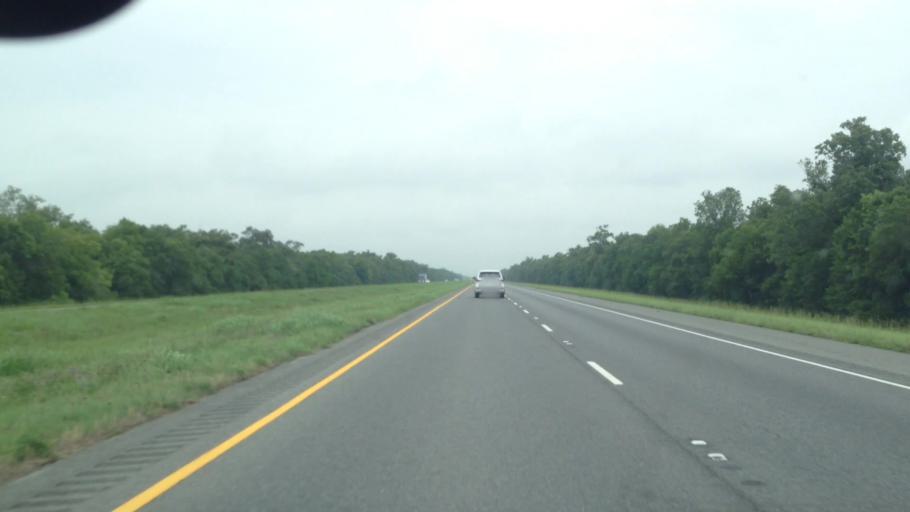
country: US
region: Louisiana
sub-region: Evangeline Parish
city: Ville Platte
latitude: 30.7384
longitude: -92.1380
